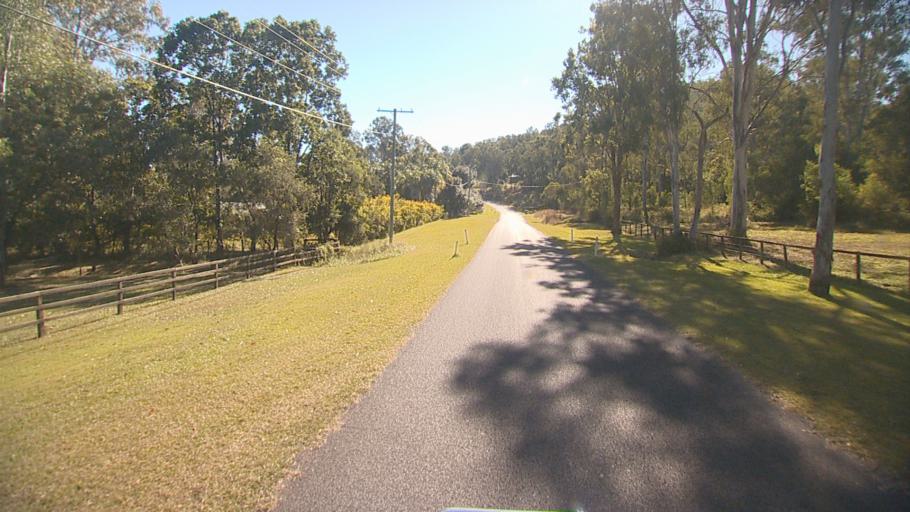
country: AU
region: Queensland
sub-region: Logan
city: Windaroo
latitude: -27.7818
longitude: 153.1480
